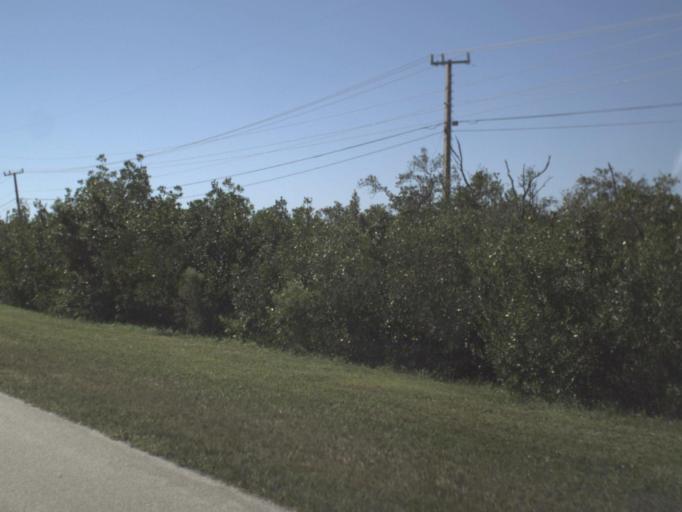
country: US
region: Florida
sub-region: Collier County
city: Marco
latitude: 26.0028
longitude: -81.7018
